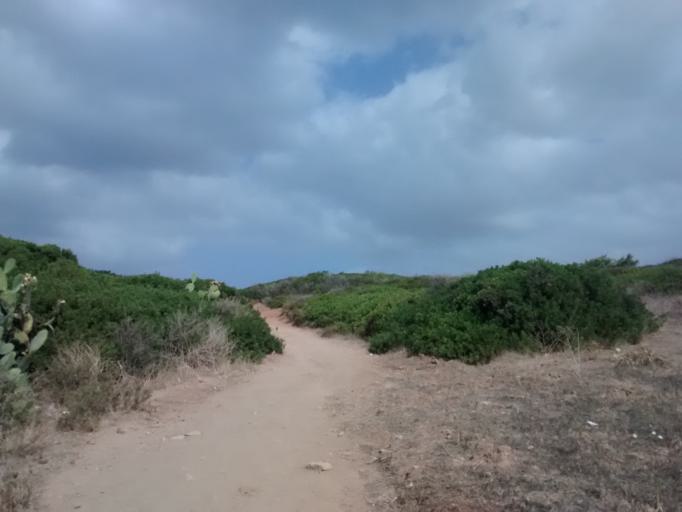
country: IT
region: Sardinia
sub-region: Provincia di Oristano
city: Narbolia
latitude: 40.0938
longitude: 8.4903
